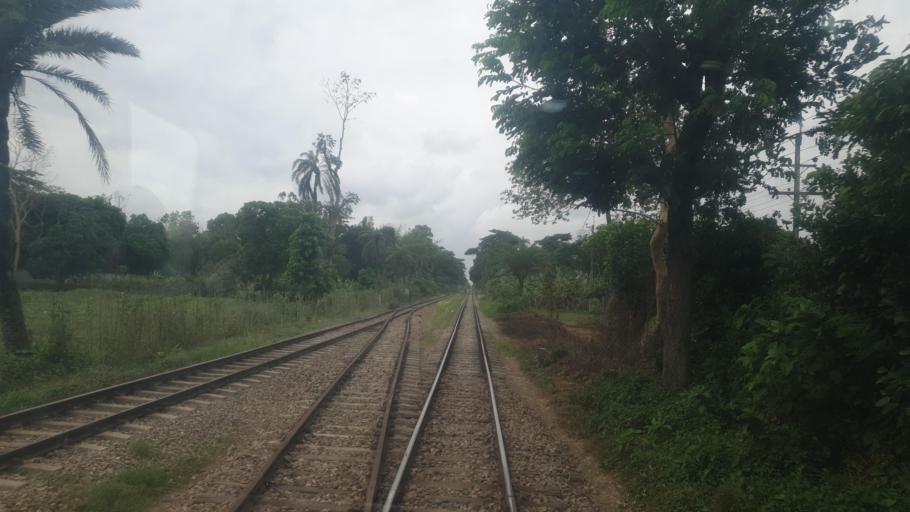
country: BD
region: Chittagong
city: Fatikchari
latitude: 22.6809
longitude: 91.6329
